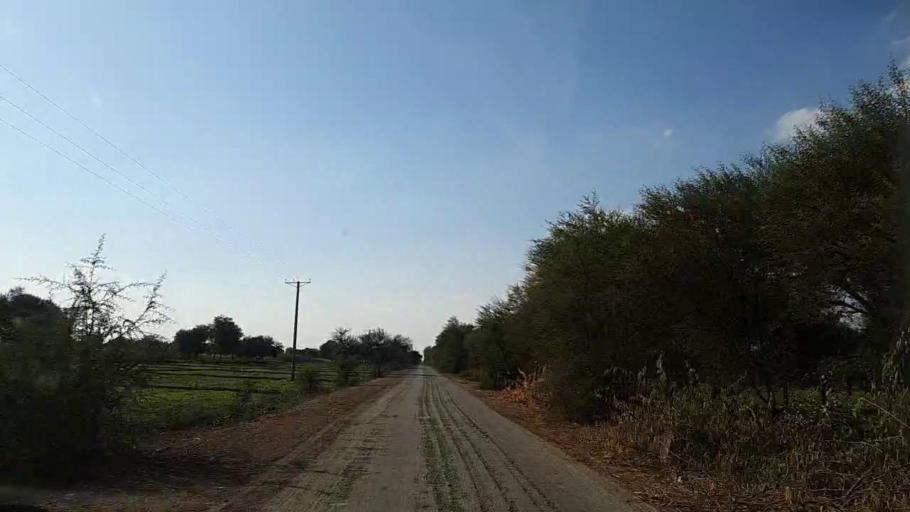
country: PK
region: Sindh
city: Pithoro
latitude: 25.6480
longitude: 69.3167
